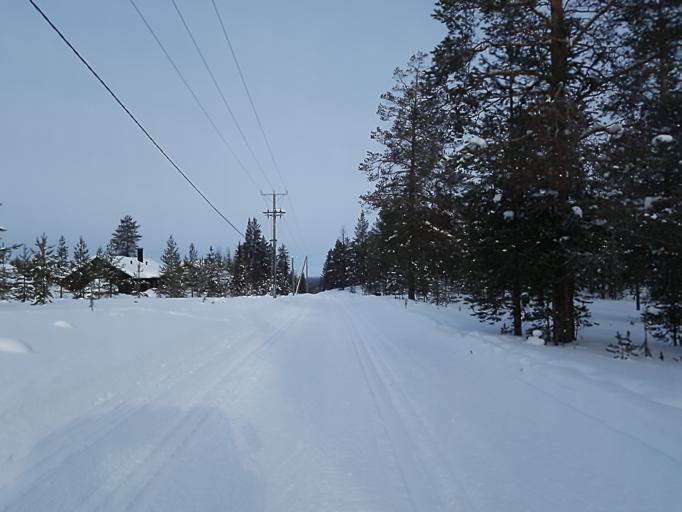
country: FI
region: Lapland
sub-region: Tunturi-Lappi
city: Kolari
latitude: 67.5948
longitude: 24.1616
